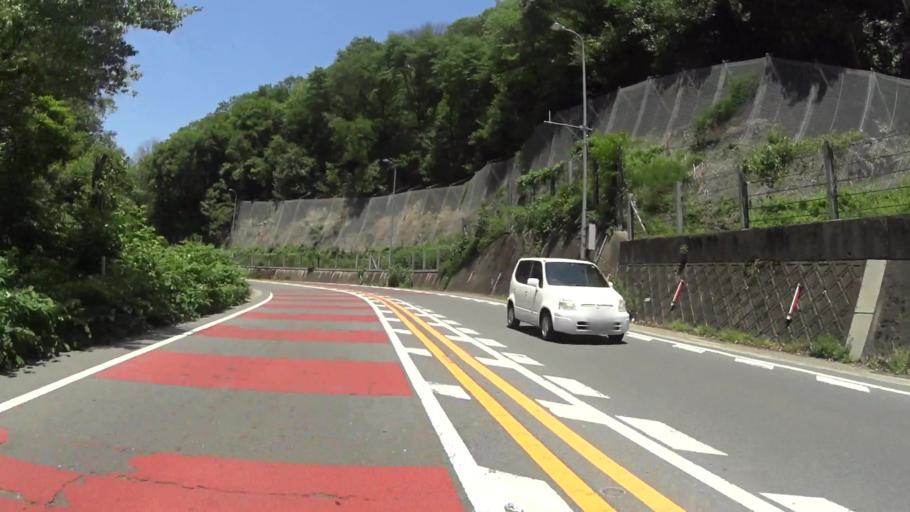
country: JP
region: Kyoto
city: Muko
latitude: 34.9901
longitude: 135.6526
